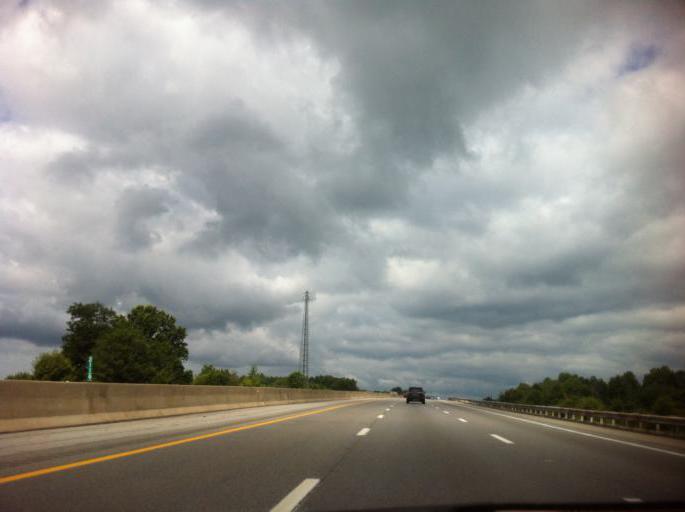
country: US
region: Ohio
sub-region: Trumbull County
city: Newton Falls
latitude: 41.1838
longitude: -80.9308
